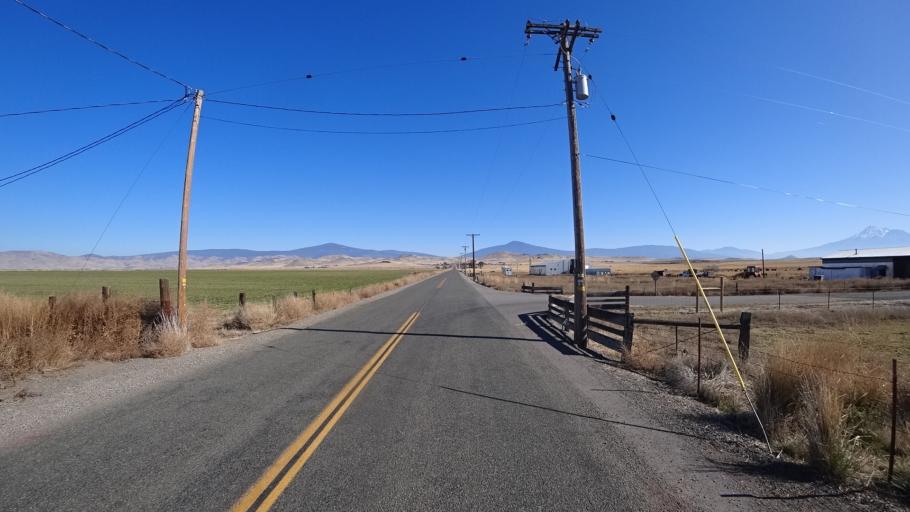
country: US
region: California
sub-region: Siskiyou County
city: Montague
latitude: 41.7561
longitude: -122.4860
